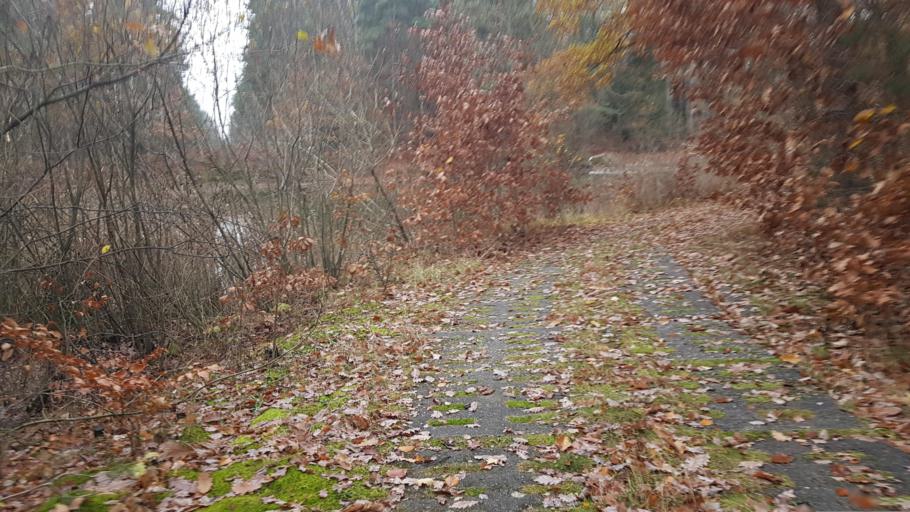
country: DE
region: Brandenburg
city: Crinitz
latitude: 51.7518
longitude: 13.7884
